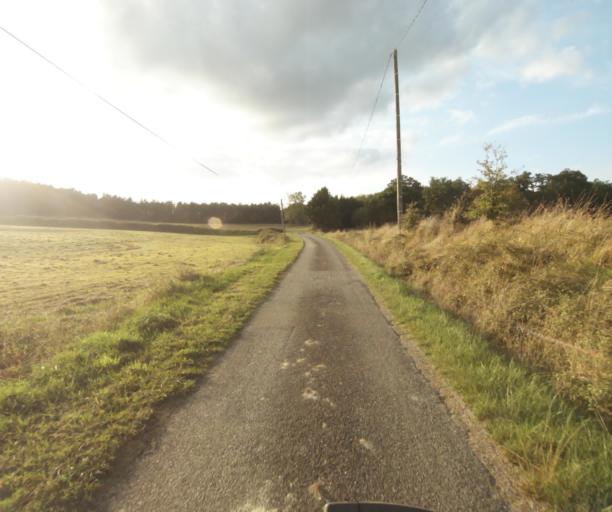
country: FR
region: Midi-Pyrenees
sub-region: Departement de la Haute-Garonne
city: Launac
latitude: 43.8297
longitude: 1.1245
